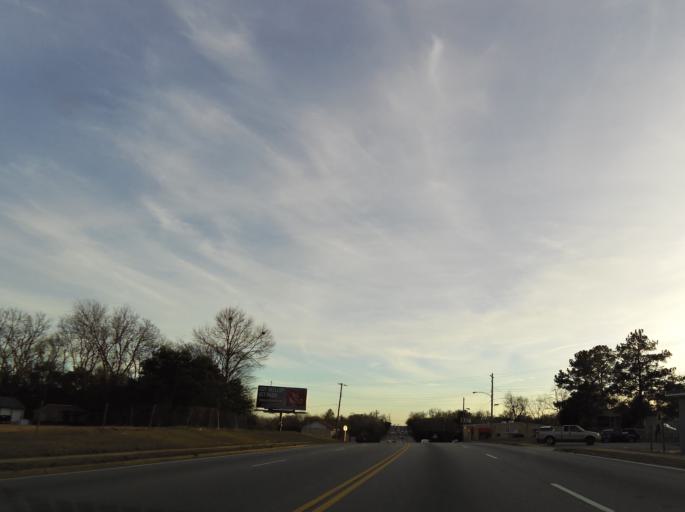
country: US
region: Georgia
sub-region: Bibb County
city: Macon
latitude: 32.8172
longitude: -83.6400
